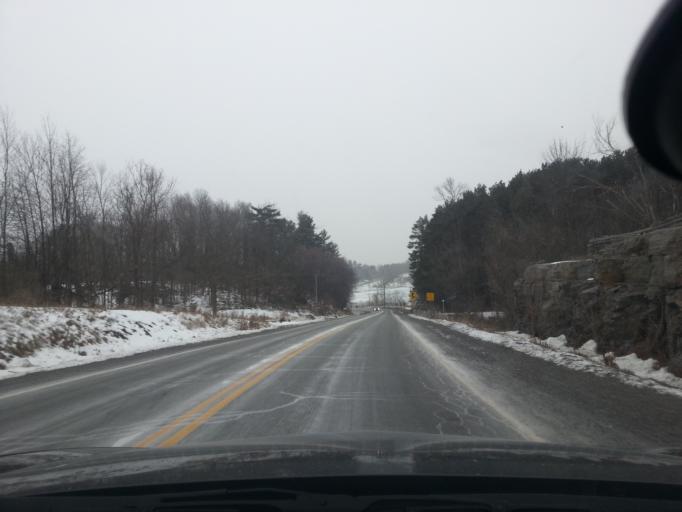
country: CA
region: Ontario
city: Arnprior
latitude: 45.3341
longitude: -76.2834
